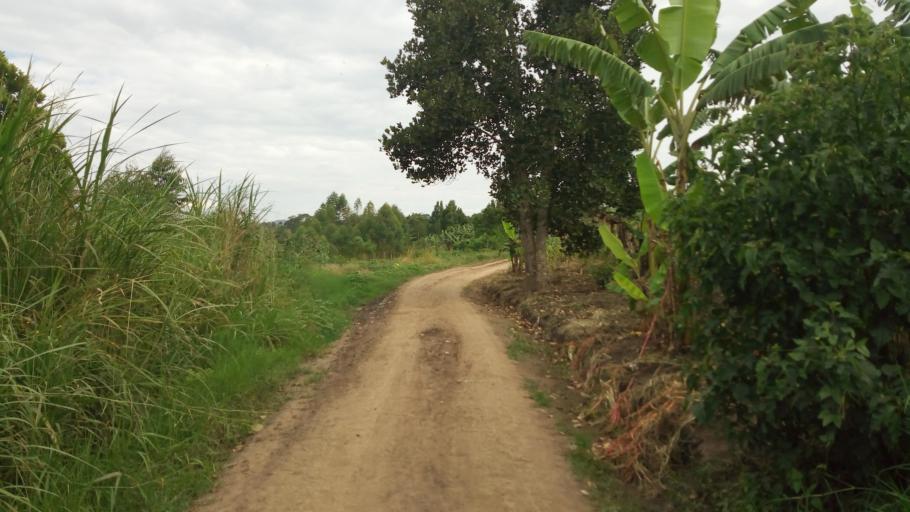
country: UG
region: Central Region
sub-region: Kiboga District
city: Kiboga
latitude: 0.7608
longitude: 31.6970
